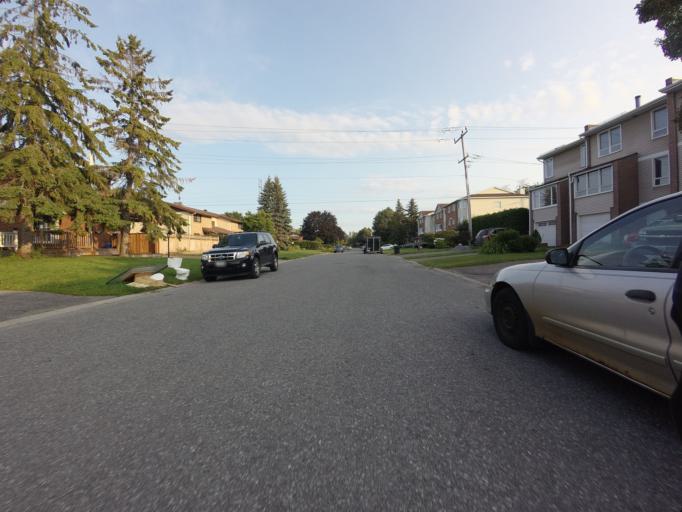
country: CA
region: Ontario
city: Bells Corners
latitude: 45.3321
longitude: -75.7495
